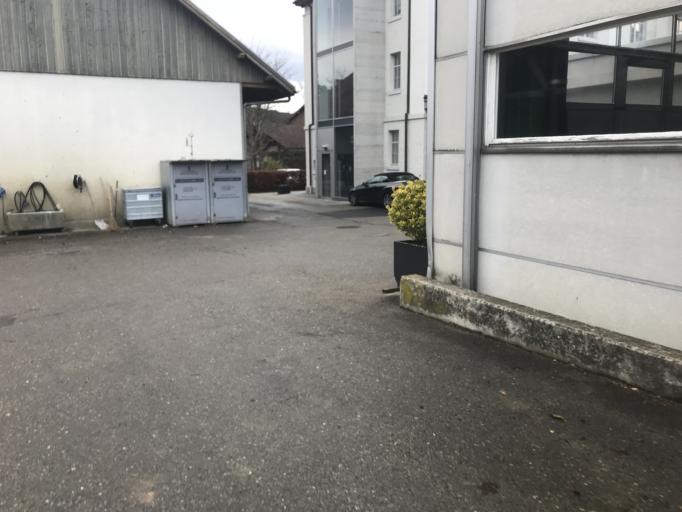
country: CH
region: Schaffhausen
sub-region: Bezirk Stein
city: Stein am Rhein
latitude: 47.6605
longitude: 8.8644
